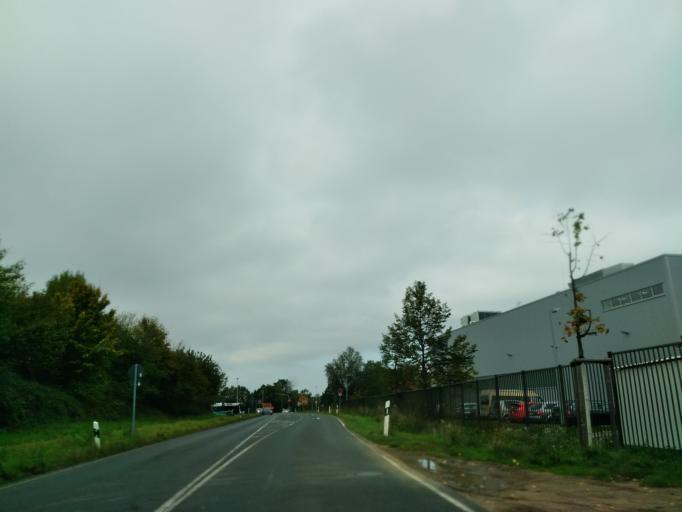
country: DE
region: North Rhine-Westphalia
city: Sankt Augustin
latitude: 50.7514
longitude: 7.1588
